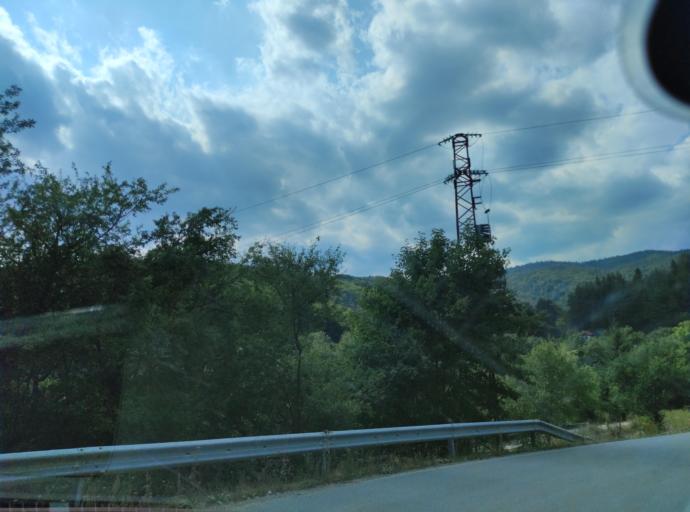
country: BG
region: Blagoevgrad
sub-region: Obshtina Belitsa
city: Belitsa
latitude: 42.0219
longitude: 23.5749
